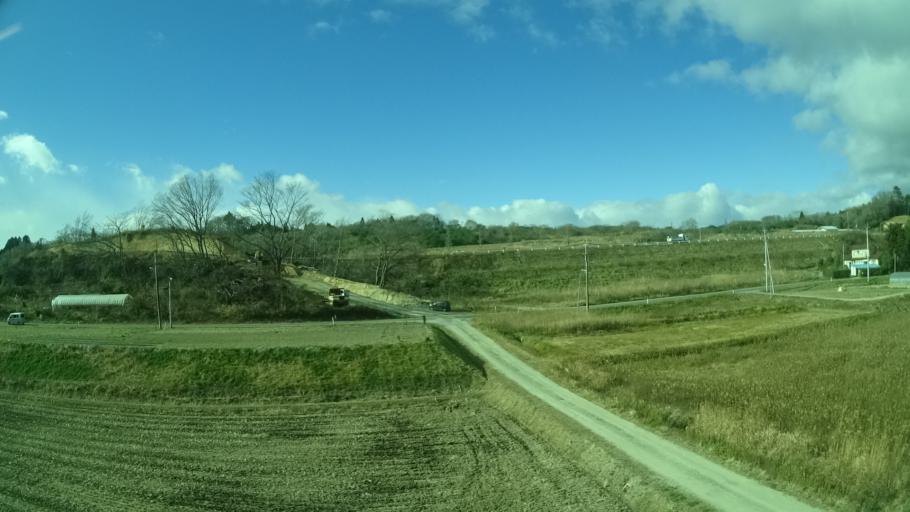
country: JP
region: Miyagi
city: Watari
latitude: 37.9304
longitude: 140.8984
